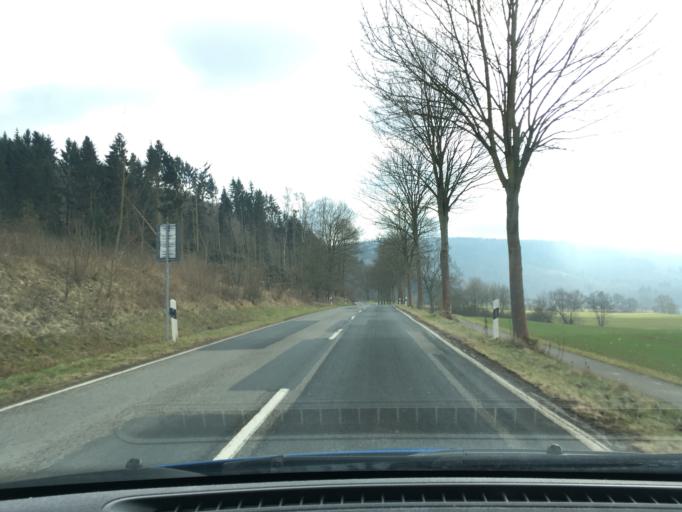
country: DE
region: Lower Saxony
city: Buhren
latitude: 51.5344
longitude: 9.6239
